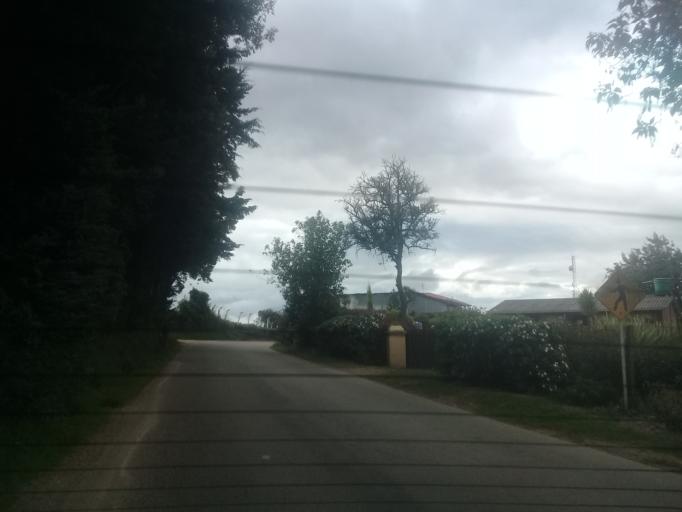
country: CO
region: Cundinamarca
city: Subachoque
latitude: 4.9319
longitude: -74.1343
